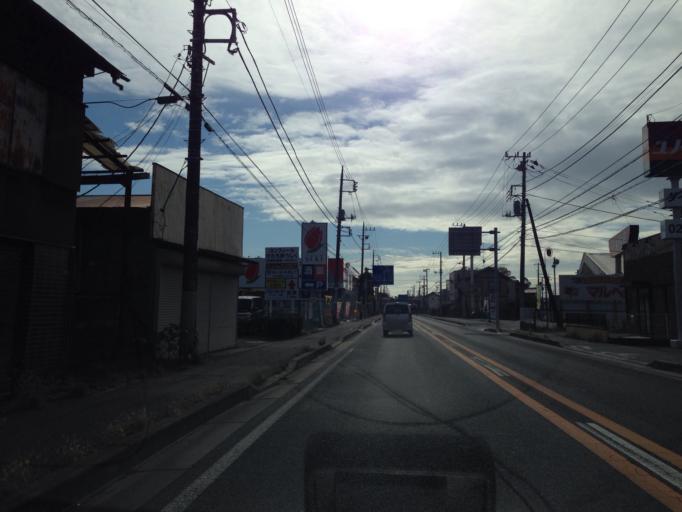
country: JP
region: Ibaraki
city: Naka
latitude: 36.0326
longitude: 140.1616
